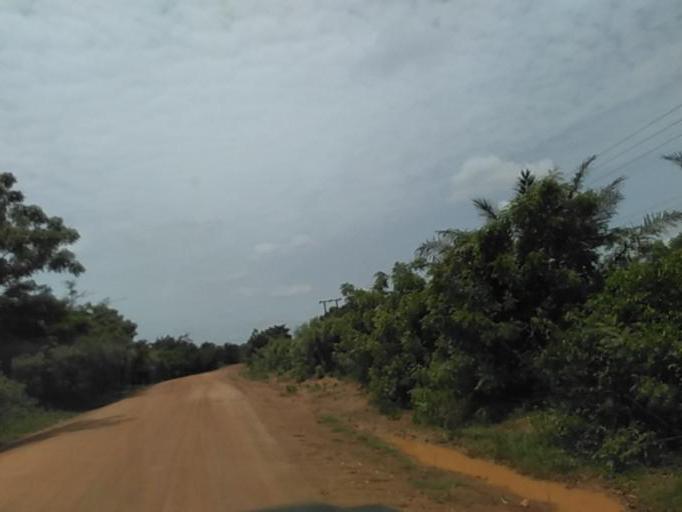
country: GH
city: Akropong
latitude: 6.0623
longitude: 0.2891
